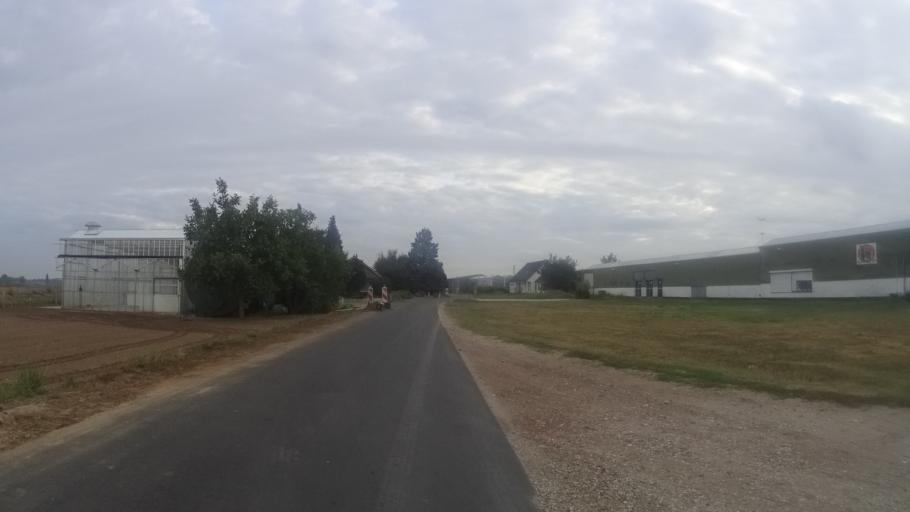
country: NL
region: Limburg
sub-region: Gemeente Venlo
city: Arcen
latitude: 51.4296
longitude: 6.1617
